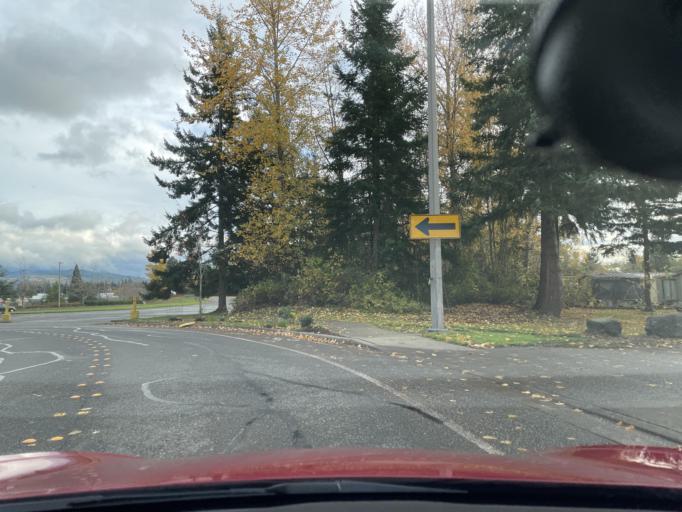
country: US
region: Washington
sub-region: Whatcom County
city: Bellingham
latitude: 48.7879
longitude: -122.4970
